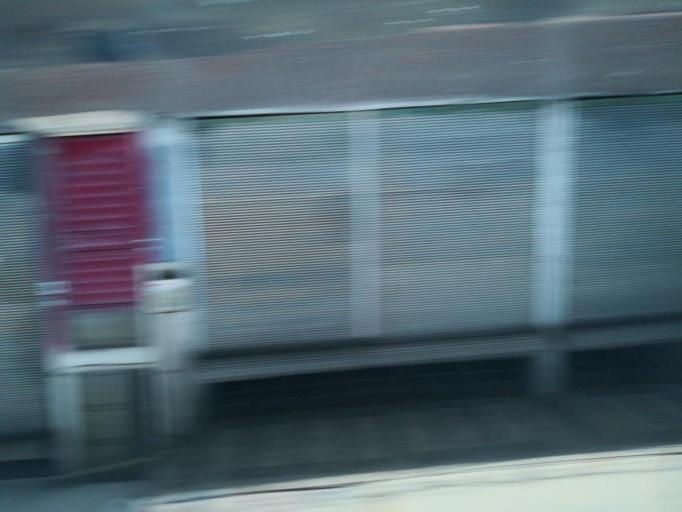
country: TR
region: Adana
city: Seyhan
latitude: 36.9983
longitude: 35.2798
